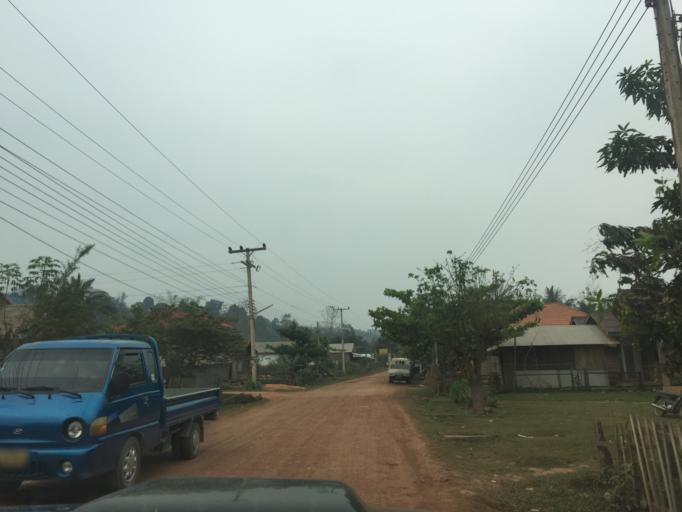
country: TH
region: Loei
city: Pak Chom
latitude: 18.5469
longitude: 101.6030
